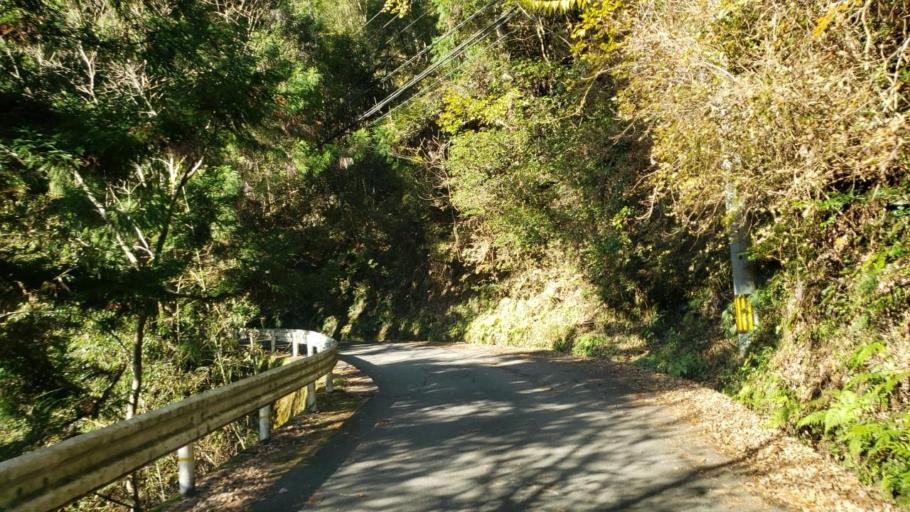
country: JP
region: Tokushima
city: Wakimachi
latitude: 33.9884
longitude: 134.0047
